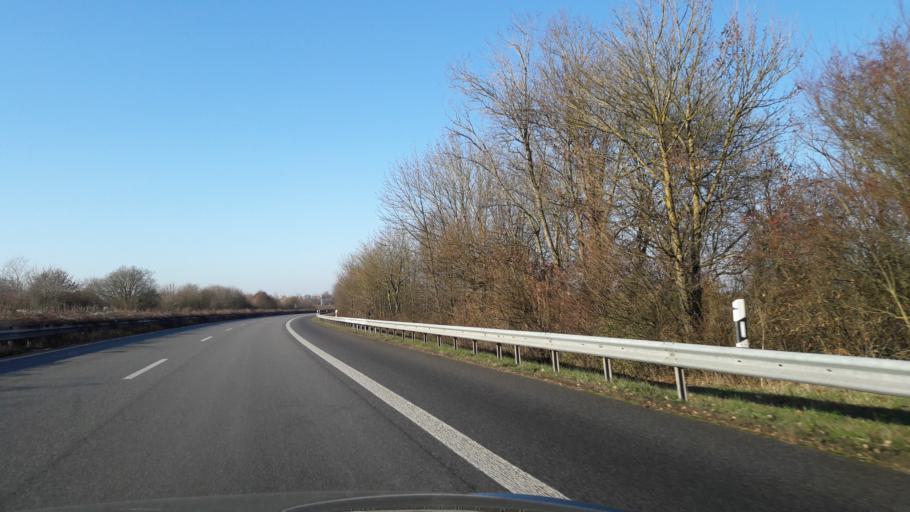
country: DE
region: Rheinland-Pfalz
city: Contwig
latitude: 49.2309
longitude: 7.4134
